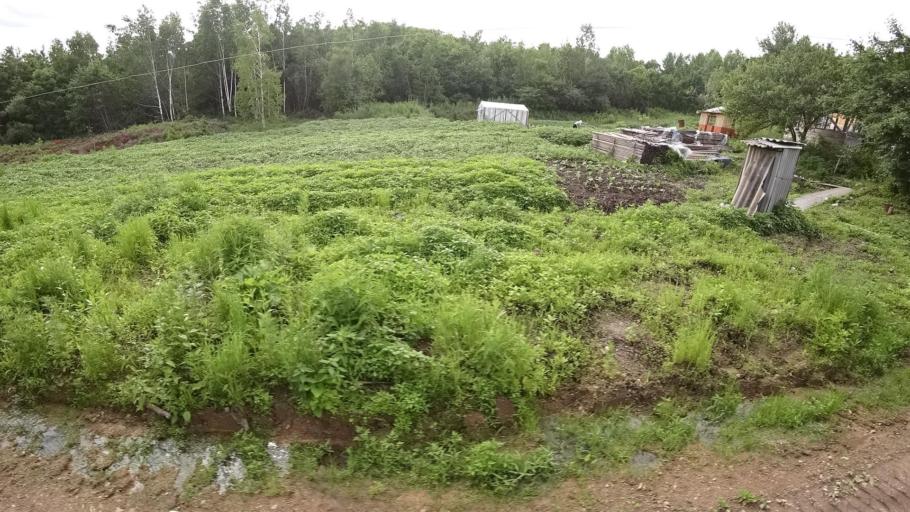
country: RU
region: Khabarovsk Krai
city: Litovko
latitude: 49.3595
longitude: 135.1778
